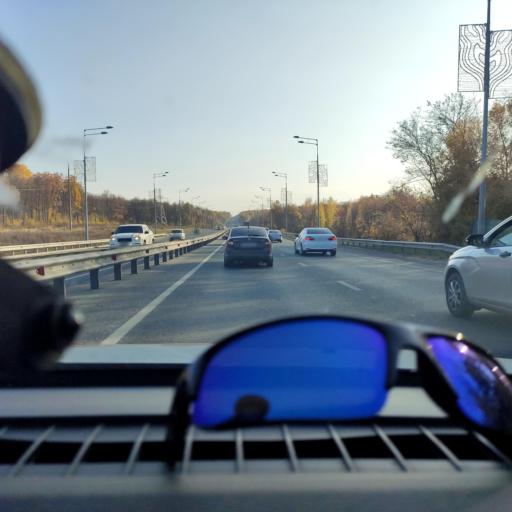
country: RU
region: Samara
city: Novosemeykino
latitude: 53.3390
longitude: 50.2325
